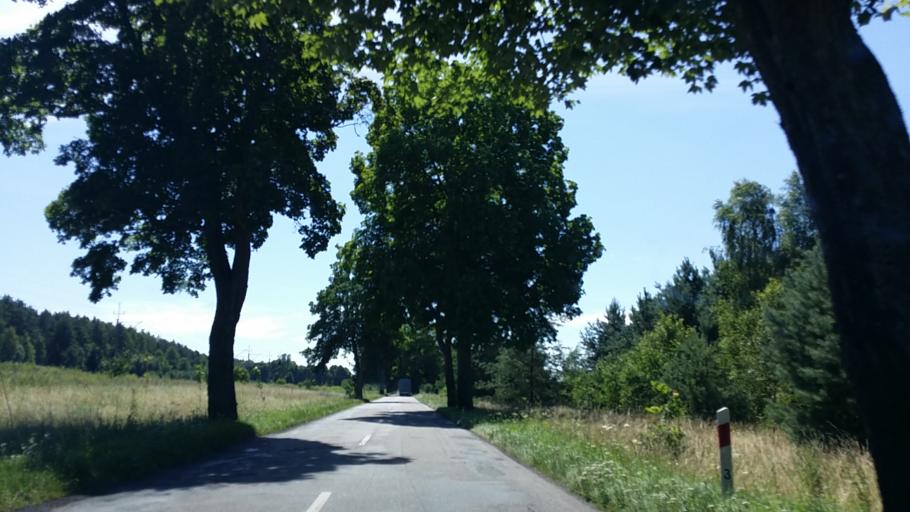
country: PL
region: West Pomeranian Voivodeship
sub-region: Powiat lobeski
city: Lobez
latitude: 53.6550
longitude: 15.6453
